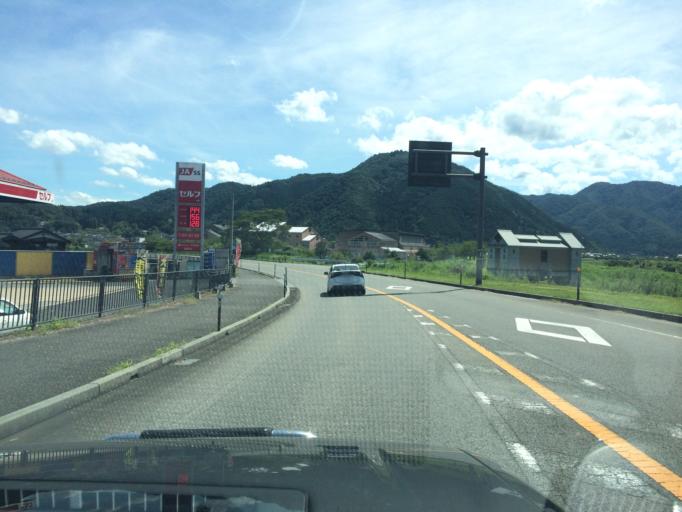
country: JP
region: Hyogo
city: Toyooka
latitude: 35.4693
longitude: 134.8663
